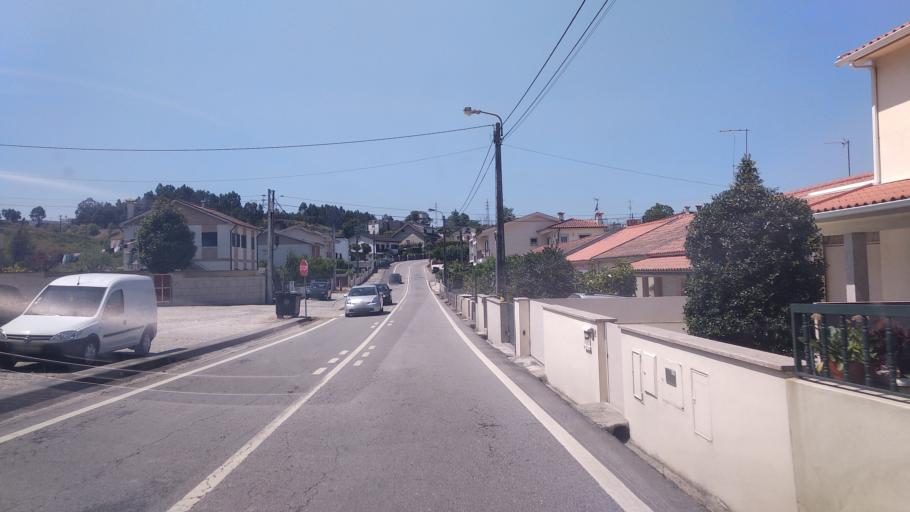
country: PT
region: Braga
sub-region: Braga
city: Braga
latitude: 41.5736
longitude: -8.4194
